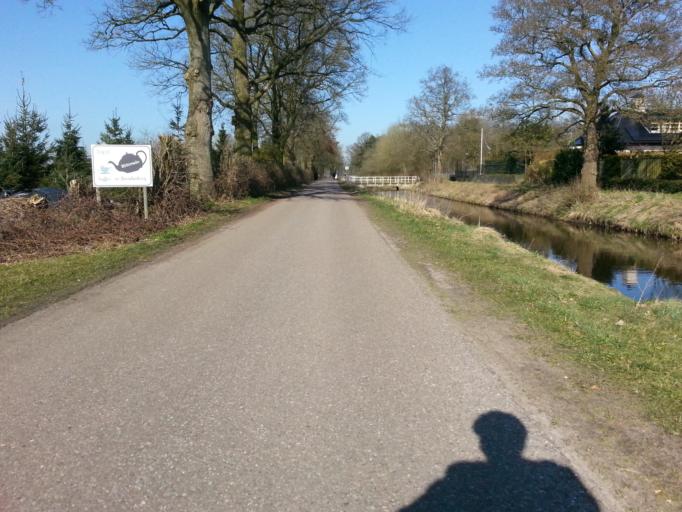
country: NL
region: Utrecht
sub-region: Gemeente Woudenberg
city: Woudenberg
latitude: 52.0867
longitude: 5.4021
